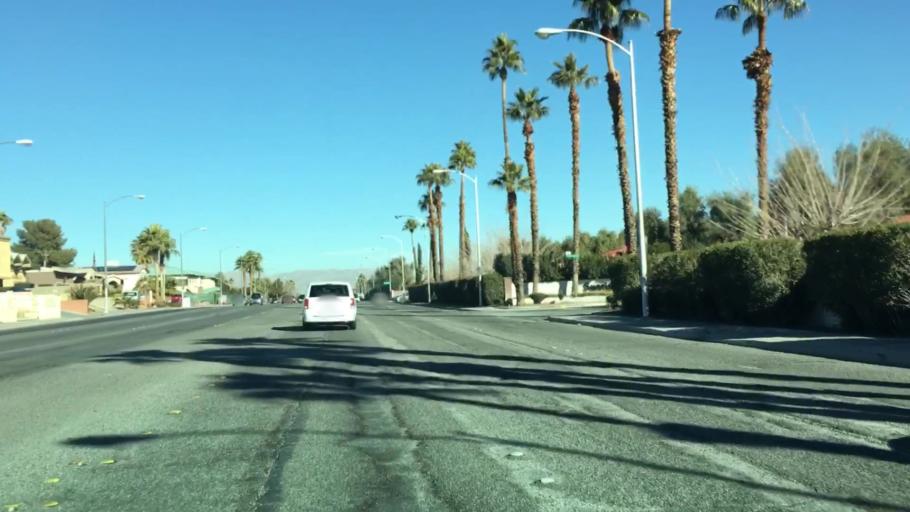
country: US
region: Nevada
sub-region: Clark County
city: Winchester
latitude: 36.1247
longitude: -115.1187
